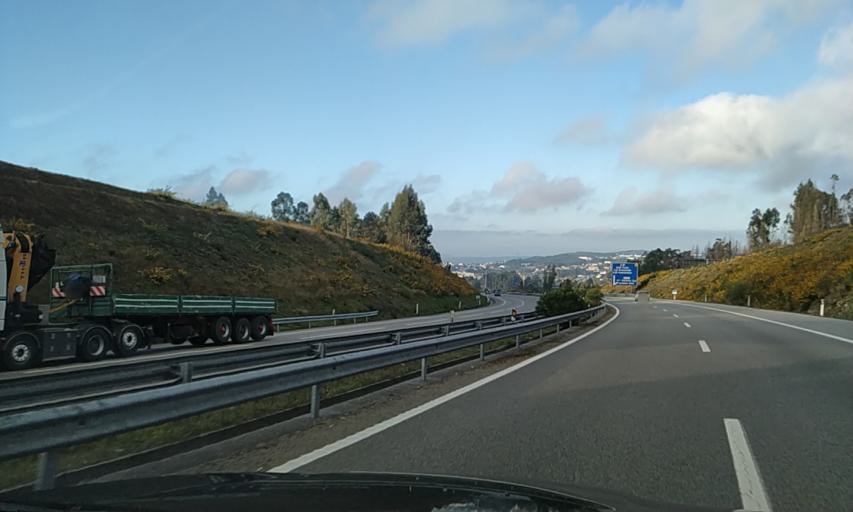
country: PT
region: Porto
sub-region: Pacos de Ferreira
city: Pacos de Ferreira
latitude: 41.2647
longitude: -8.3828
